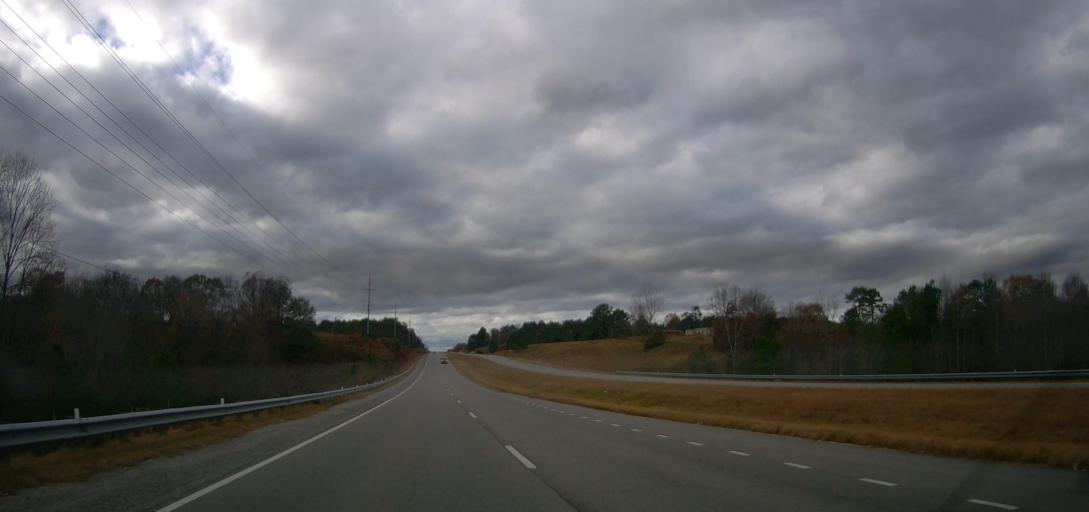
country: US
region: Alabama
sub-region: Lawrence County
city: Moulton
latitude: 34.5634
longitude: -87.3578
